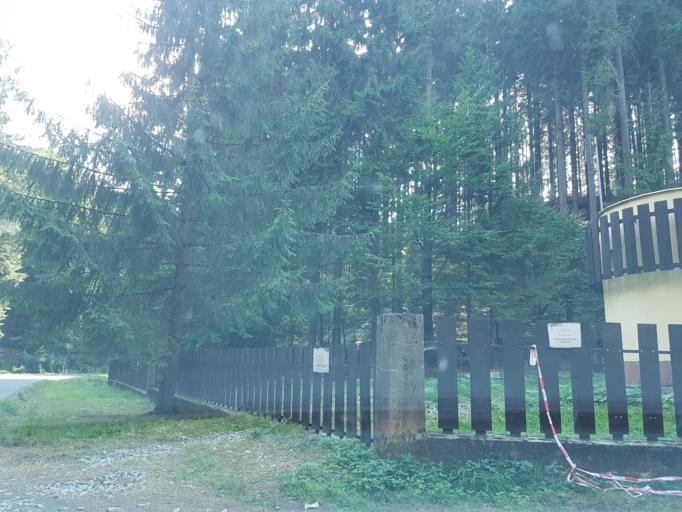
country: DE
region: Saxony
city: Sebnitz
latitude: 50.8771
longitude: 14.2854
